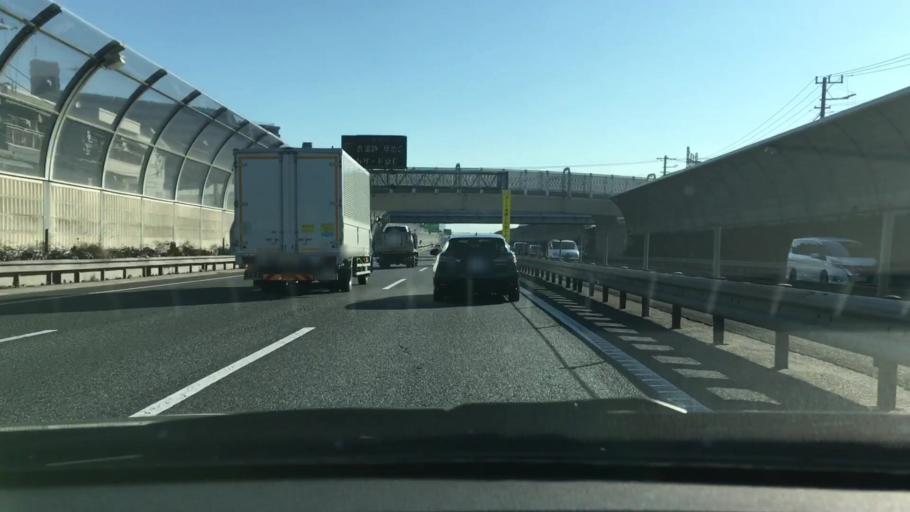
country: JP
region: Chiba
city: Funabashi
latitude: 35.7061
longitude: 139.9432
